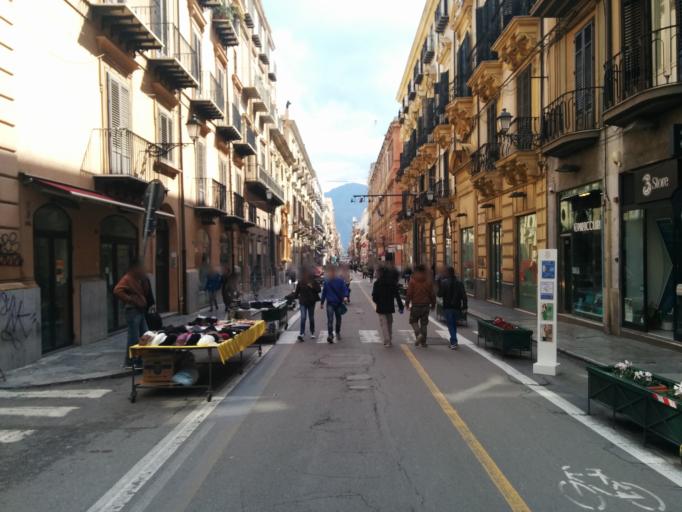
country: IT
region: Sicily
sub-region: Palermo
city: Palermo
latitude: 38.1197
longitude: 13.3589
